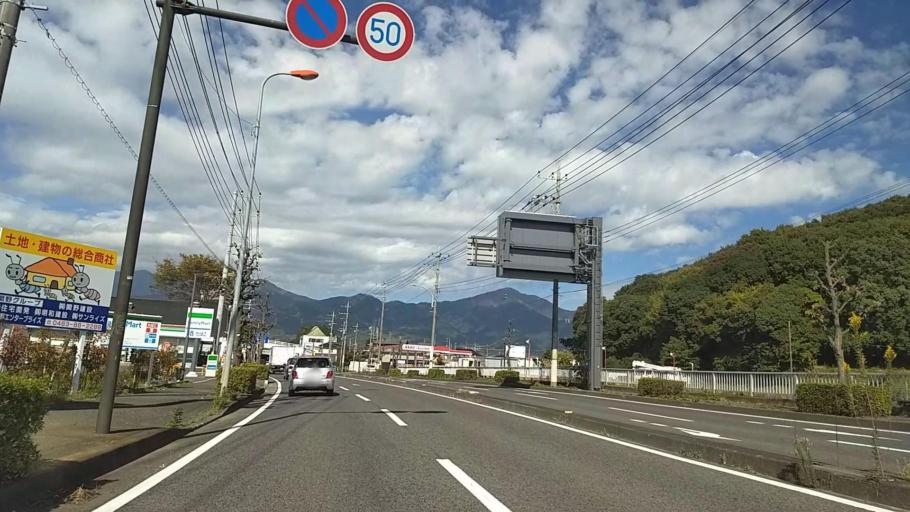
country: JP
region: Kanagawa
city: Hadano
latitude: 35.3557
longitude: 139.2362
